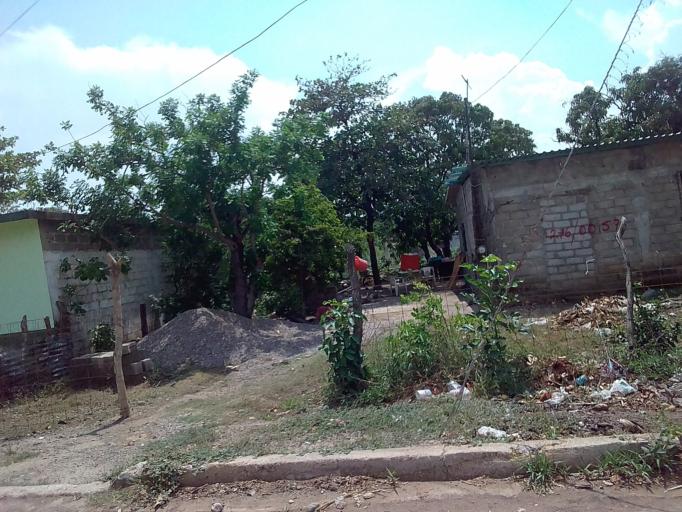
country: MX
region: Oaxaca
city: Union Hidalgo
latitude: 16.4658
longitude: -94.8288
